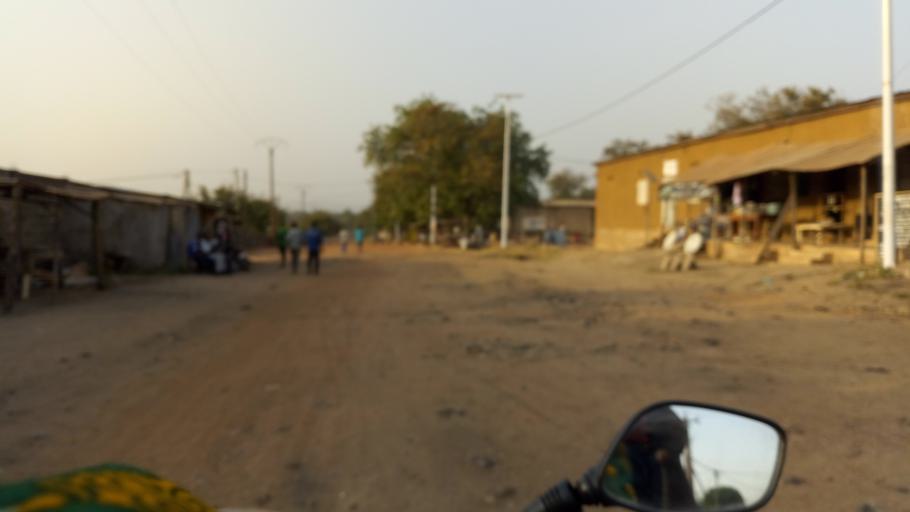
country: TG
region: Kara
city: Kara
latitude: 9.5504
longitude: 1.2001
